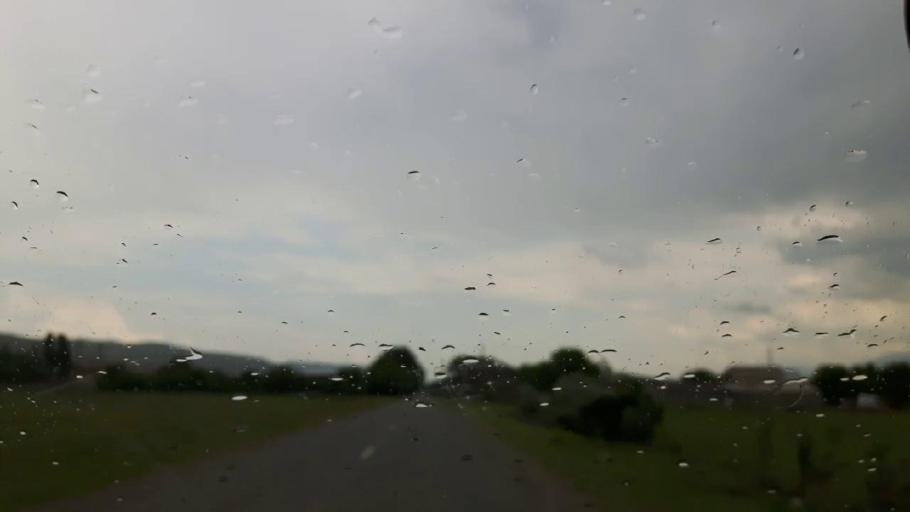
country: GE
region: Shida Kartli
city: Gori
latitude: 41.9626
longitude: 44.1932
